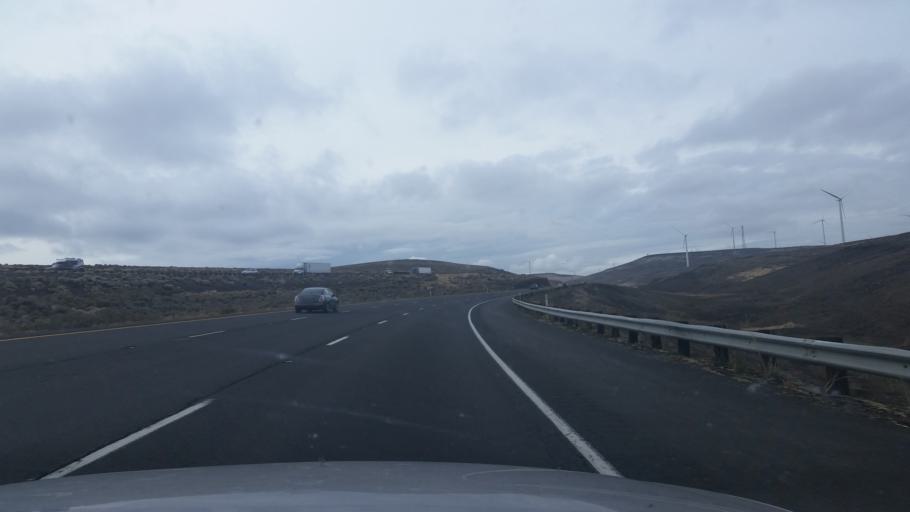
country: US
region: Washington
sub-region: Kittitas County
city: Kittitas
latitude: 46.9391
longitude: -120.1289
